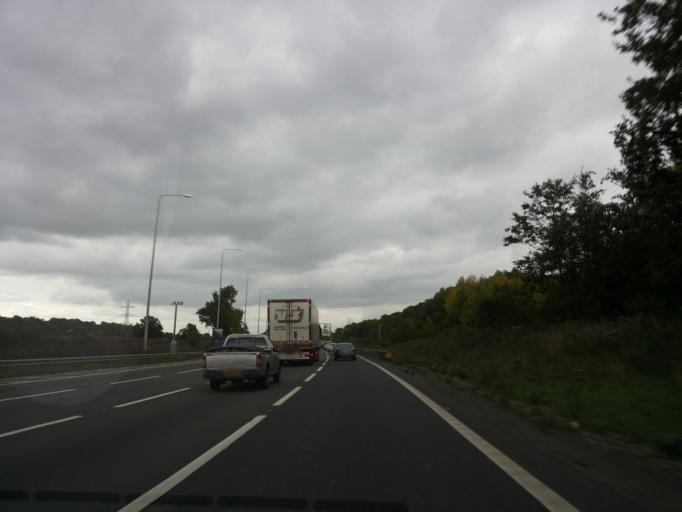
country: GB
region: England
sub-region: Greater London
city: High Barnet
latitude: 51.6845
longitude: -0.2155
